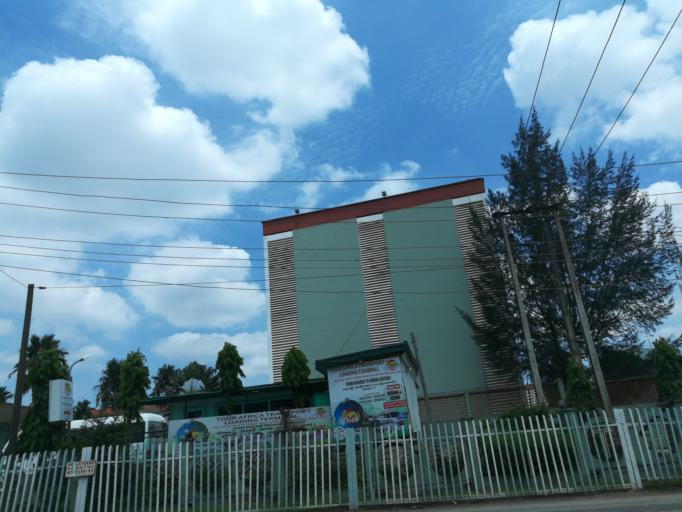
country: NG
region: Lagos
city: Ikeja
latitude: 6.6060
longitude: 3.3478
